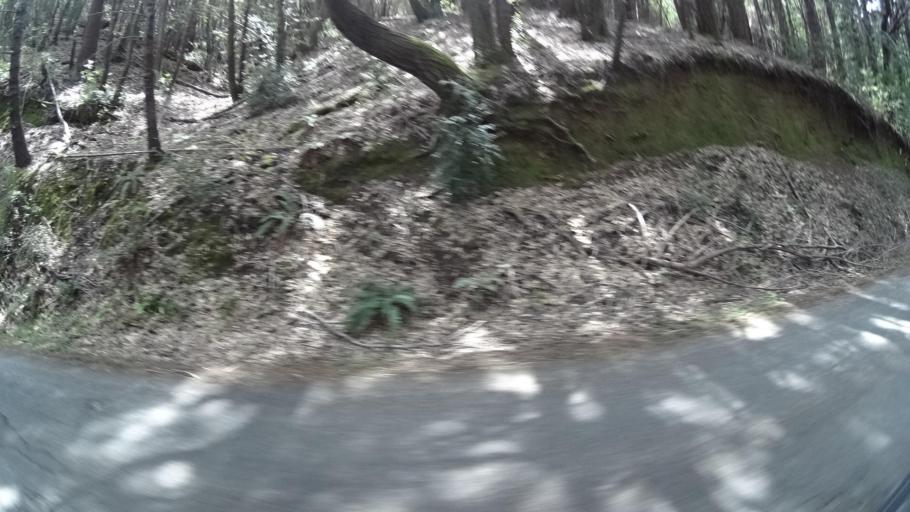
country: US
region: California
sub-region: Humboldt County
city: Redway
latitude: 40.0488
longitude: -123.9583
